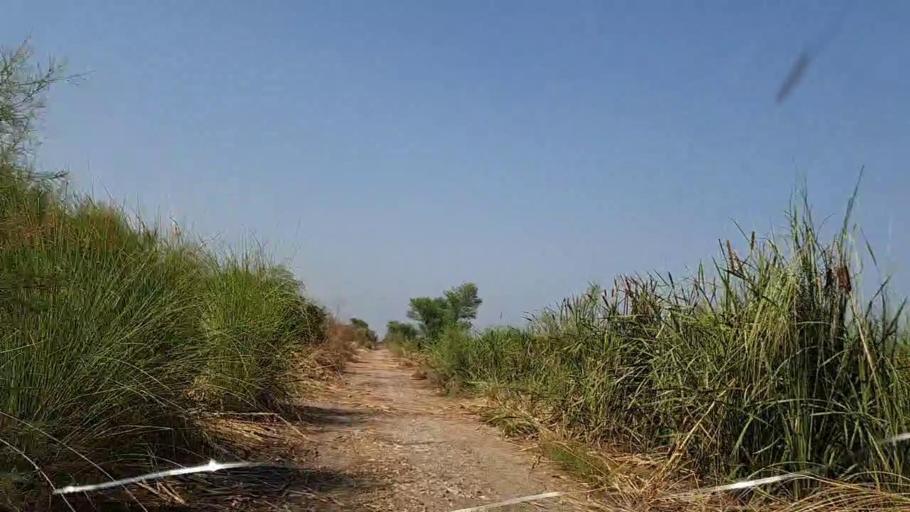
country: PK
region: Sindh
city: Khanpur
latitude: 27.6806
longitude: 69.3780
